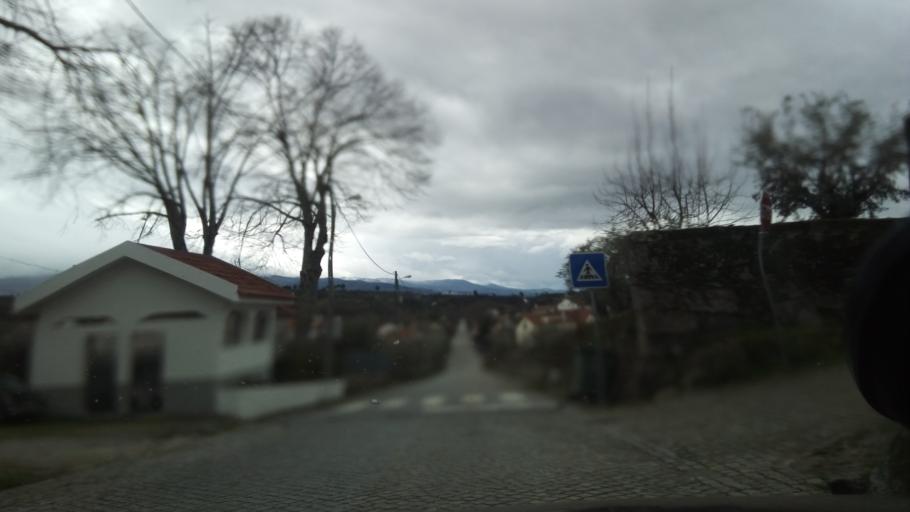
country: PT
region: Guarda
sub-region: Fornos de Algodres
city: Fornos de Algodres
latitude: 40.5891
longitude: -7.5383
